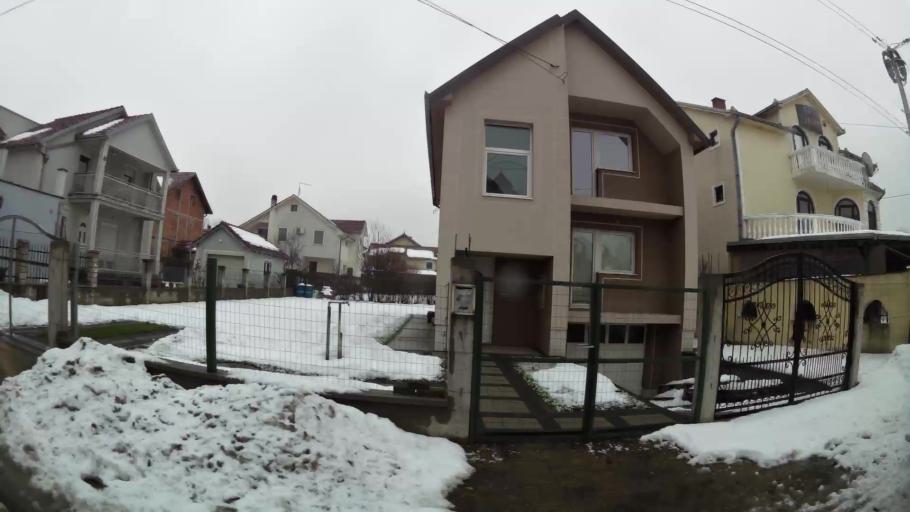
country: RS
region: Central Serbia
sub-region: Belgrade
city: Zemun
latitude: 44.8526
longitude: 20.3564
